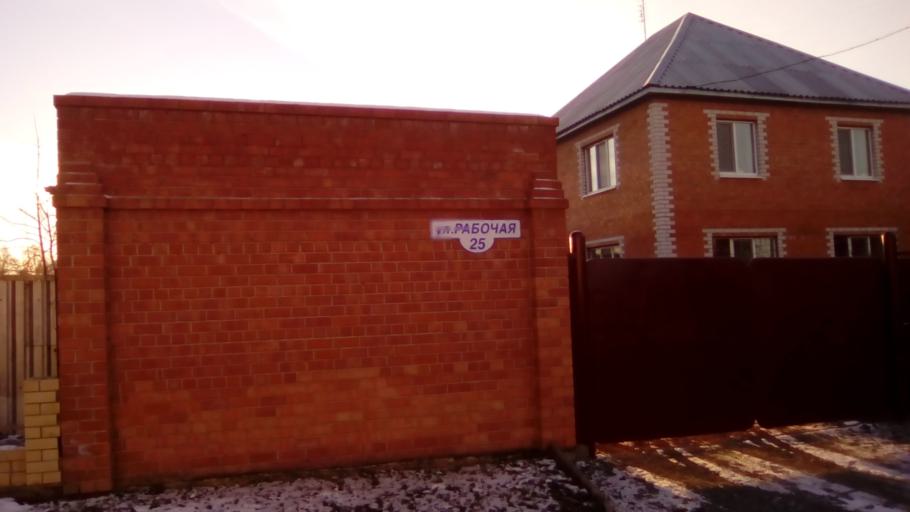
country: RU
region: Tjumen
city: Moskovskiy
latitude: 57.2218
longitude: 65.3639
